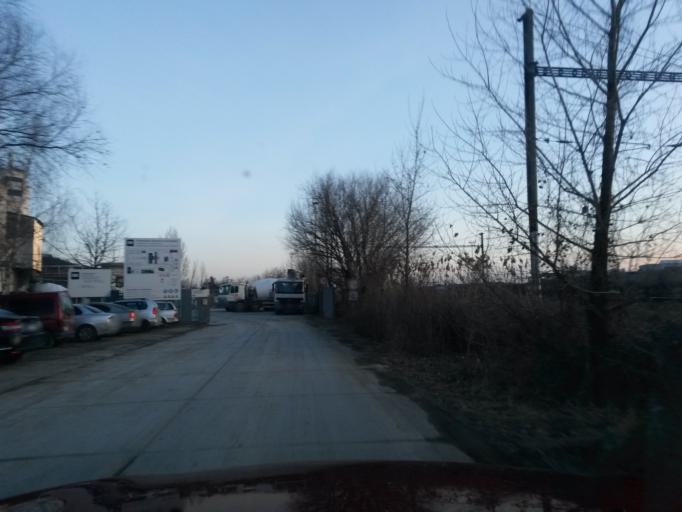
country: SK
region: Kosicky
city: Kosice
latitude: 48.7158
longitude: 21.2748
